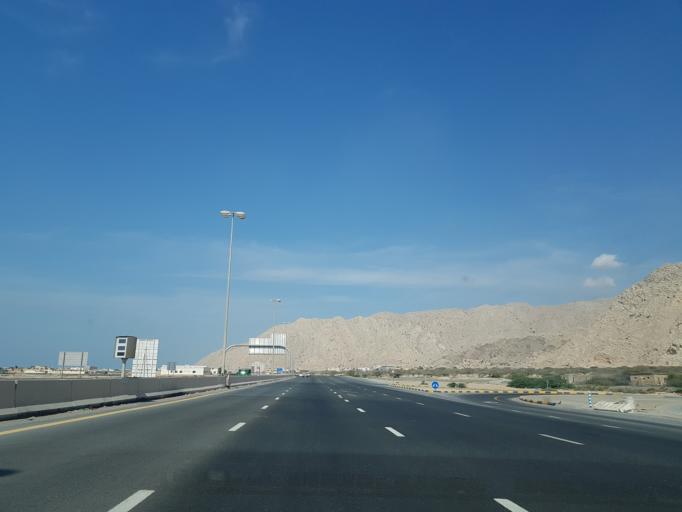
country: AE
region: Ra's al Khaymah
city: Ras al-Khaimah
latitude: 25.8406
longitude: 56.0177
